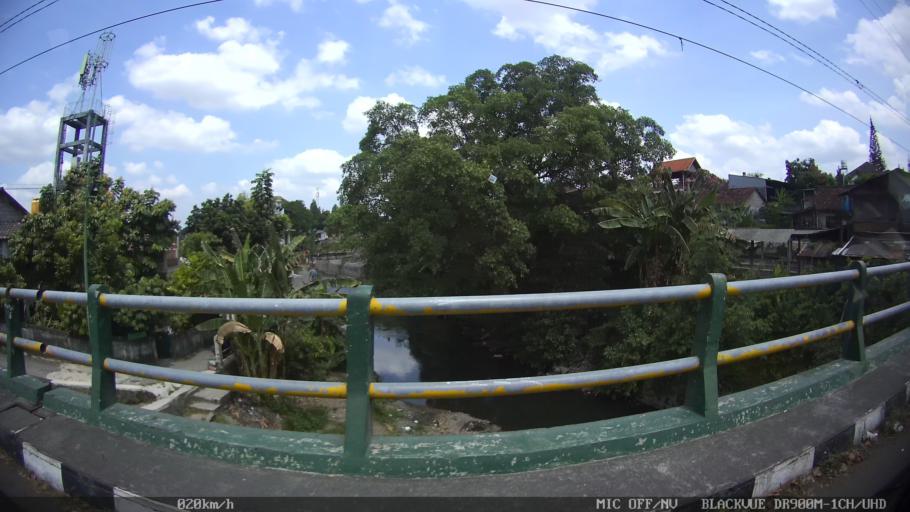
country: ID
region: Daerah Istimewa Yogyakarta
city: Kasihan
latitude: -7.8174
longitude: 110.3515
